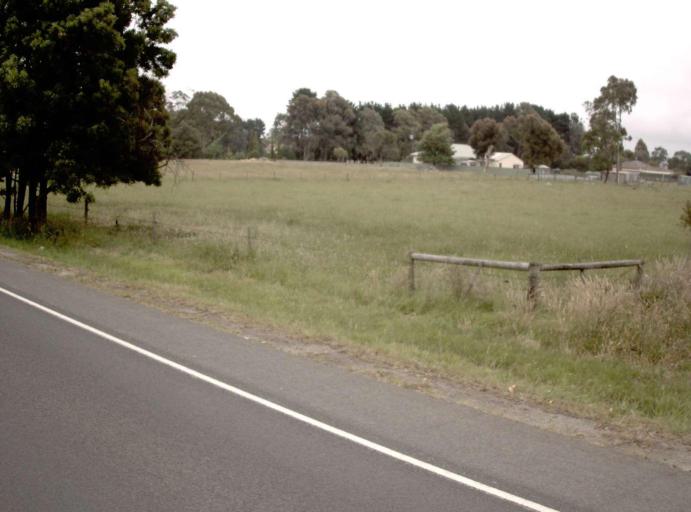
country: AU
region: Victoria
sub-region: Latrobe
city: Morwell
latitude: -38.2509
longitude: 146.4542
